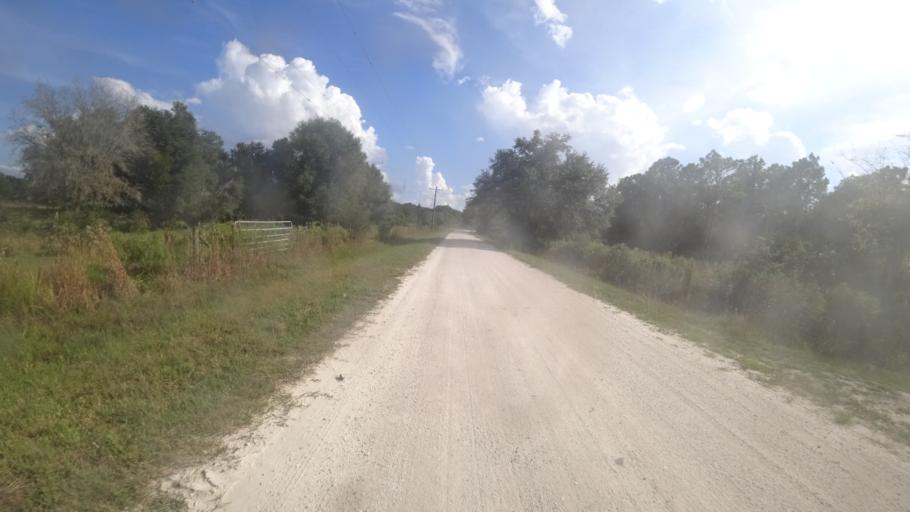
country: US
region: Florida
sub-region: Hillsborough County
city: Balm
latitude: 27.6242
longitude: -82.1206
